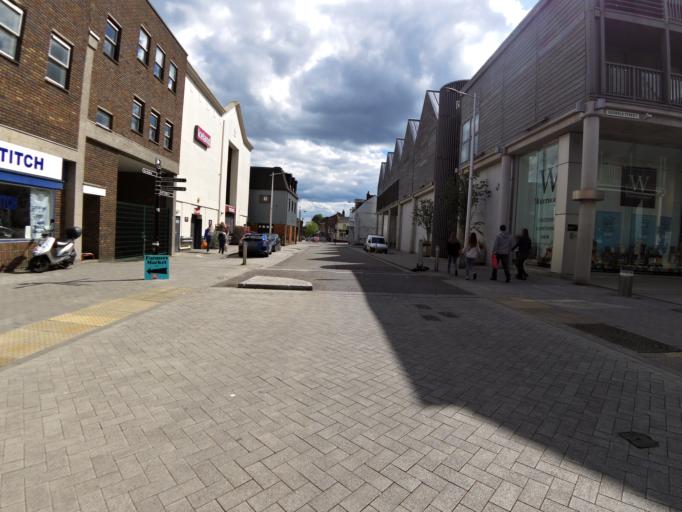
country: GB
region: England
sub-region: Suffolk
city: Bury St Edmunds
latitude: 52.2455
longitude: 0.7111
